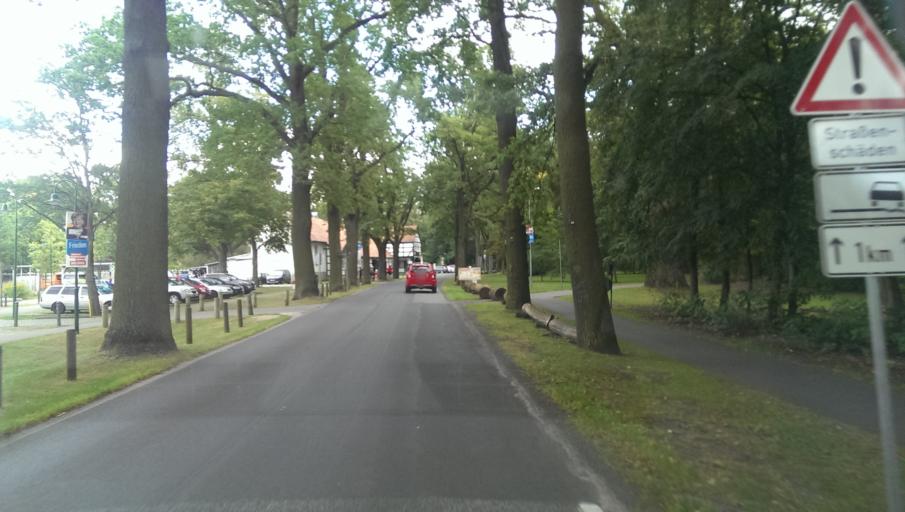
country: DE
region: Berlin
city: Falkenhagener Feld
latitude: 52.6004
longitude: 13.1367
